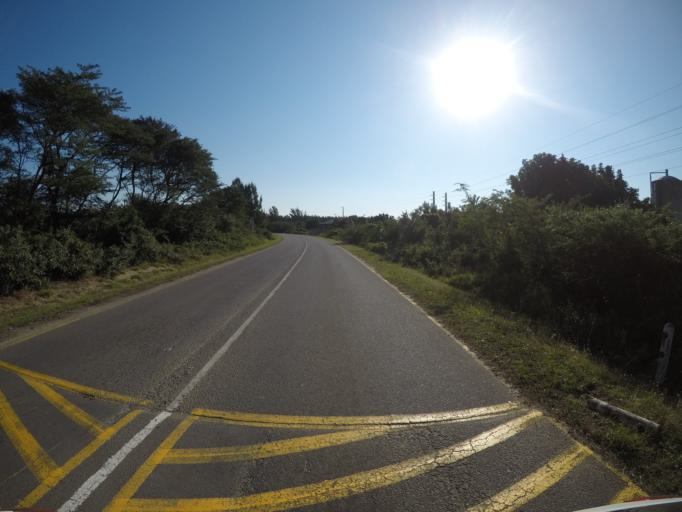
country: ZA
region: KwaZulu-Natal
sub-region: uThungulu District Municipality
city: Richards Bay
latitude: -28.7822
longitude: 32.0734
